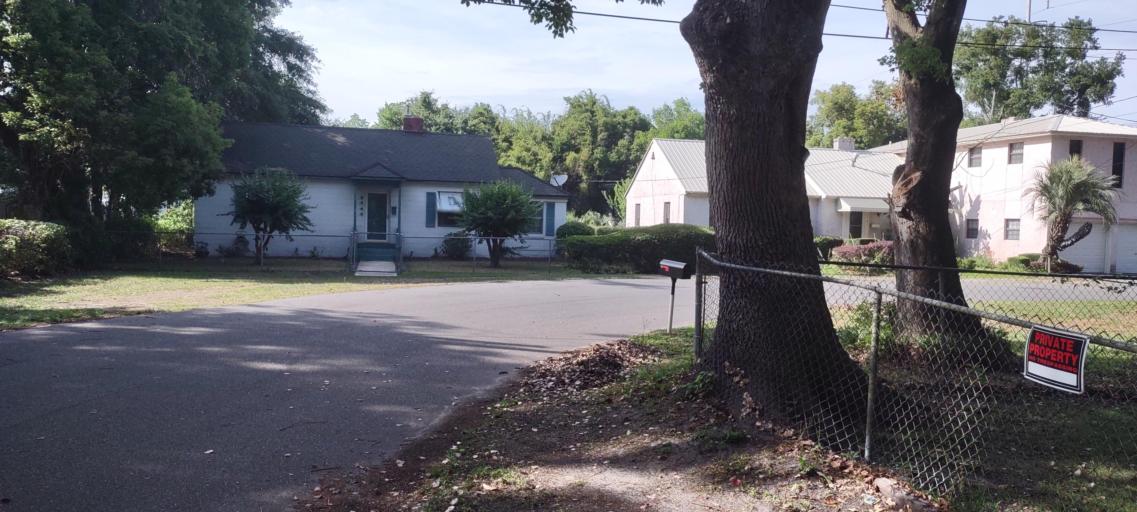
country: US
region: Georgia
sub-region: Glynn County
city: Dock Junction
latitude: 31.1820
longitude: -81.4924
